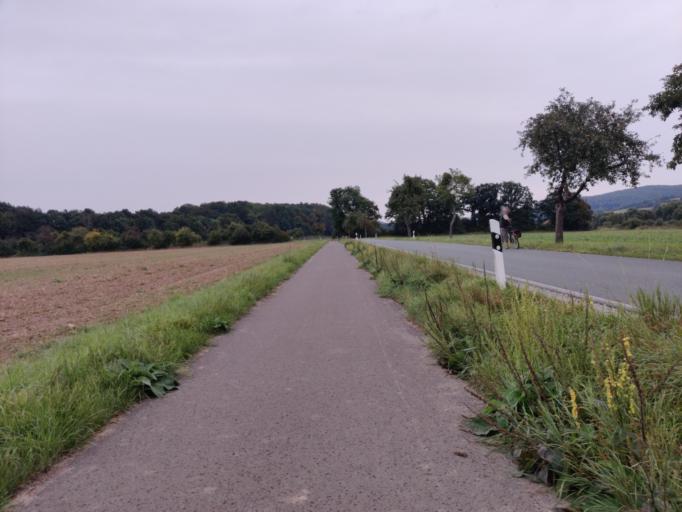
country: DE
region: Lower Saxony
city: Polle
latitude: 51.8927
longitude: 9.4169
